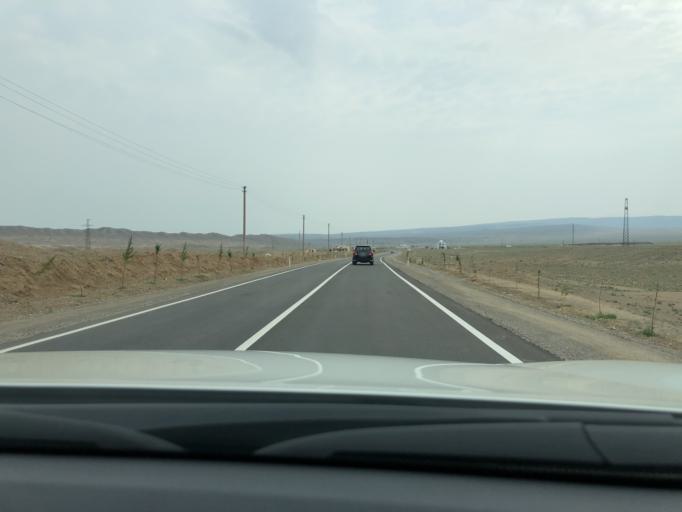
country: TJ
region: Viloyati Sughd
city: Kim
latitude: 40.1968
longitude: 70.4756
